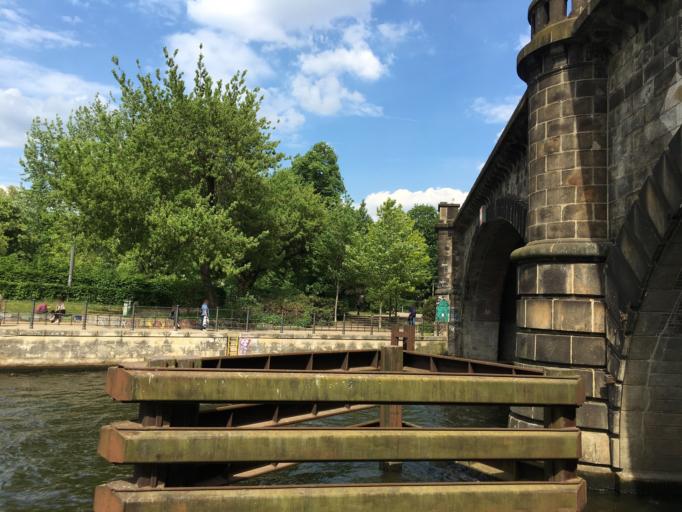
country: DE
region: Berlin
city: Mitte
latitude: 52.5219
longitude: 13.3964
